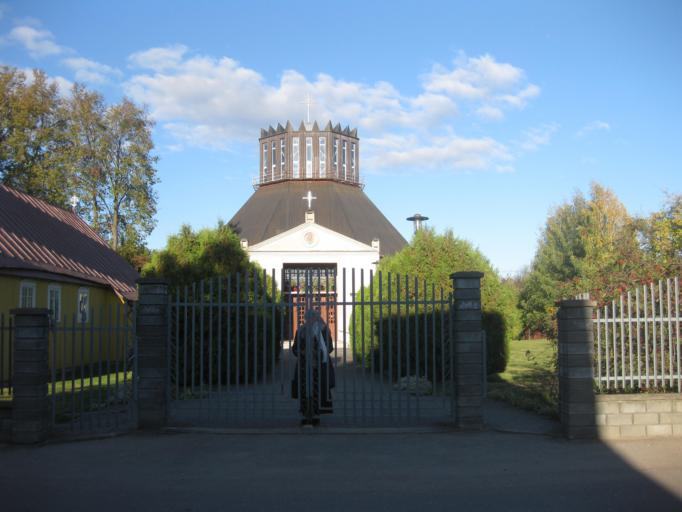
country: LT
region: Kauno apskritis
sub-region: Kaunas
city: Aleksotas
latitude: 54.8876
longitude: 23.8988
